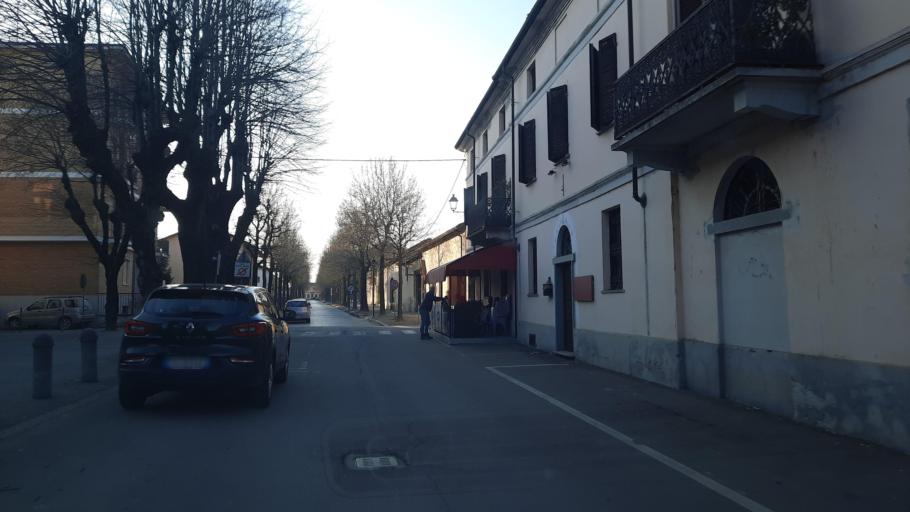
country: IT
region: Piedmont
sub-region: Provincia di Vercelli
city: Bianze
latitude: 45.3078
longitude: 8.1194
